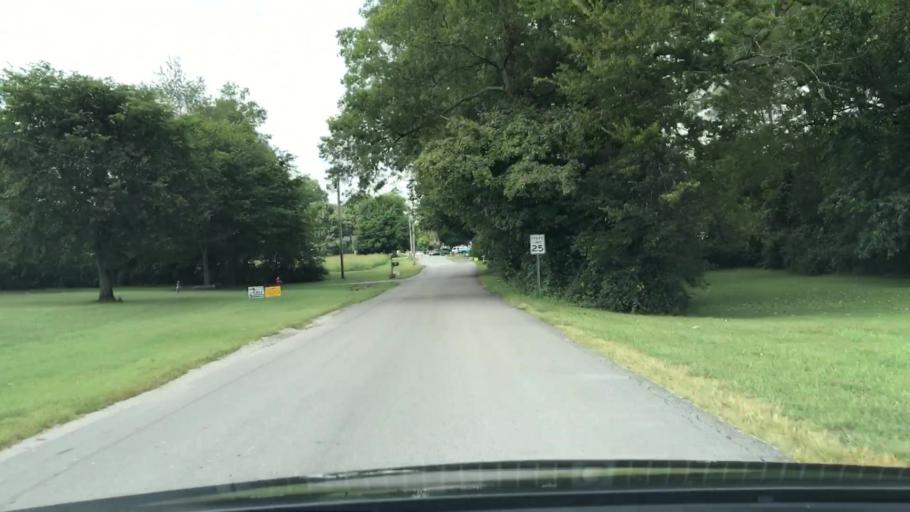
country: US
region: Kentucky
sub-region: Todd County
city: Elkton
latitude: 36.8057
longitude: -87.1497
